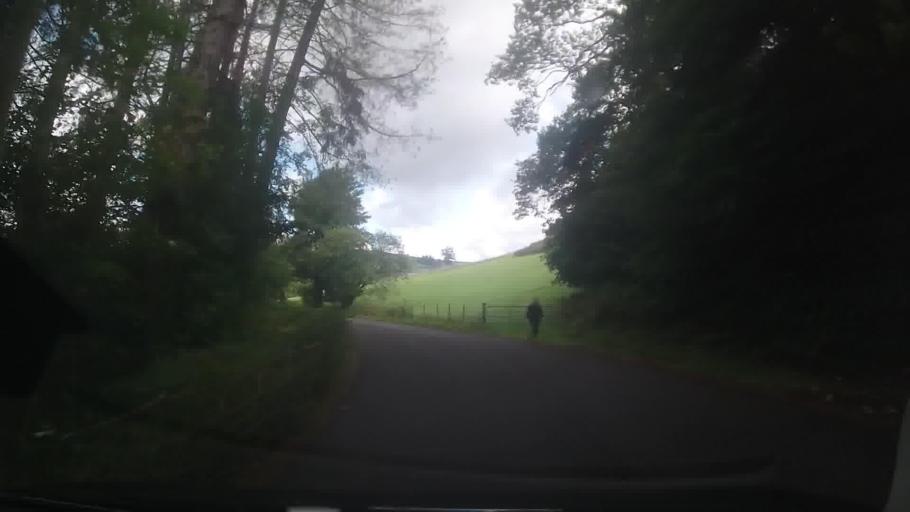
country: GB
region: Wales
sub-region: Sir Powys
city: Llangynog
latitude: 52.7664
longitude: -3.4533
